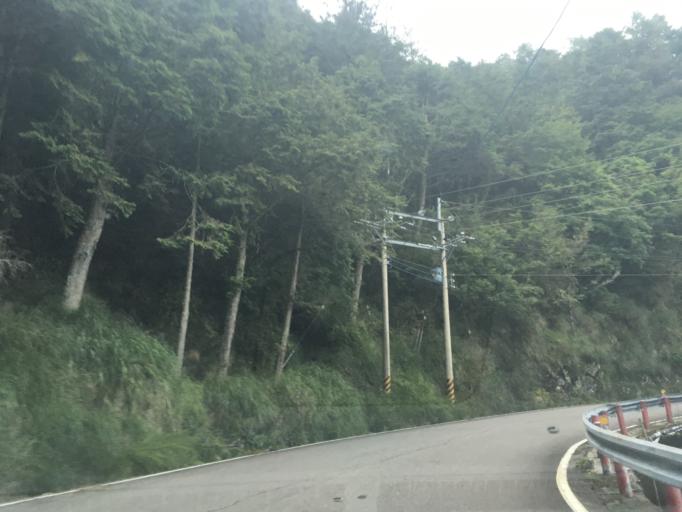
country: TW
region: Taiwan
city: Fengyuan
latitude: 24.2654
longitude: 121.0144
